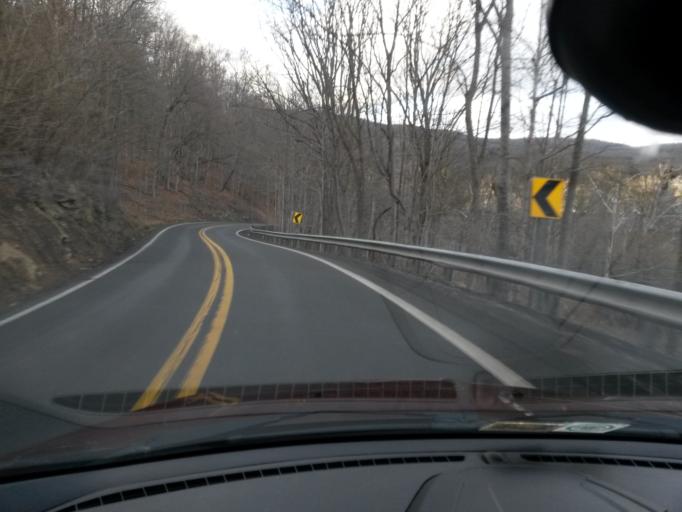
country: US
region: West Virginia
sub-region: Monroe County
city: Union
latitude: 37.5675
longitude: -80.5691
